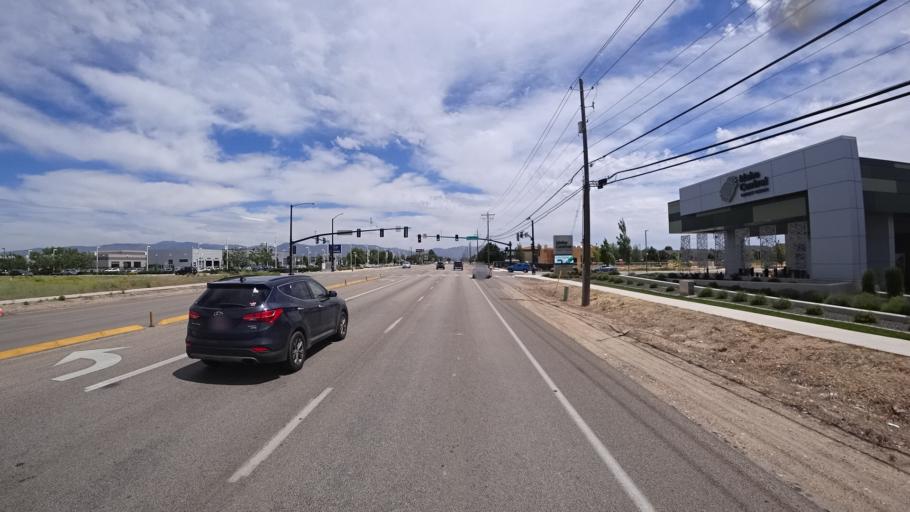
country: US
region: Idaho
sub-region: Ada County
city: Meridian
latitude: 43.6194
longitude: -116.3233
